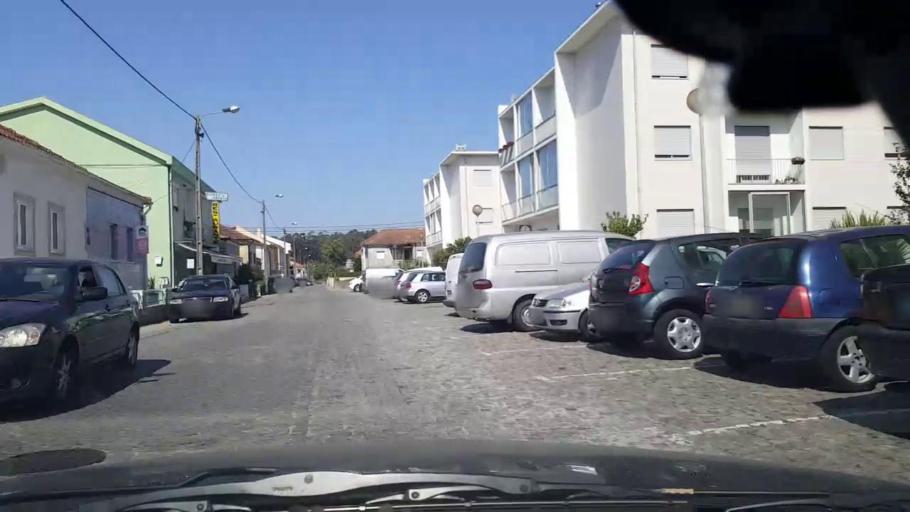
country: PT
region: Porto
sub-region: Vila do Conde
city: Vila do Conde
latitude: 41.3617
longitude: -8.7272
